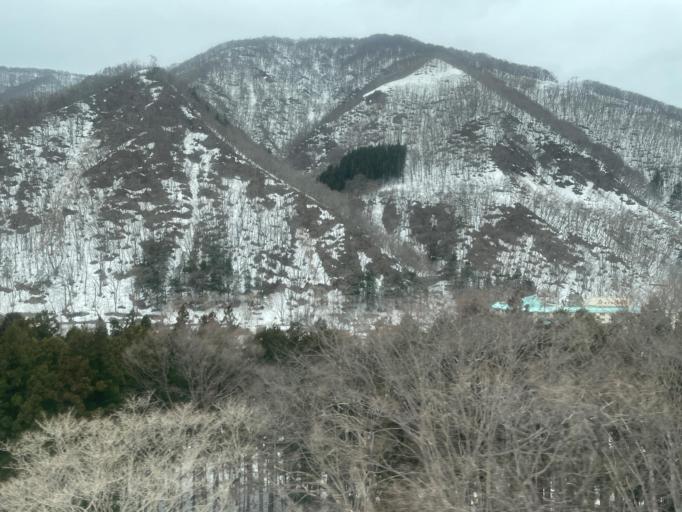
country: JP
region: Gunma
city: Numata
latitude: 36.8098
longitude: 138.9878
